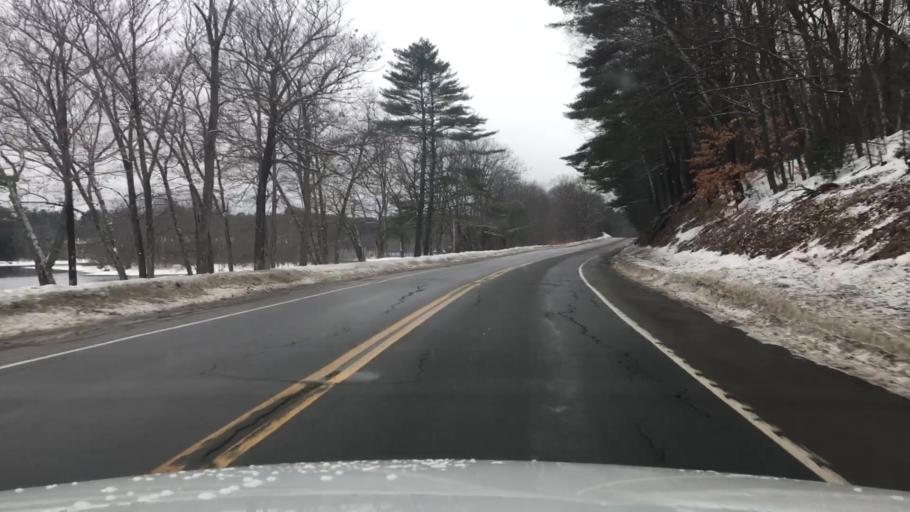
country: US
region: Maine
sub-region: Somerset County
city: Skowhegan
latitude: 44.7690
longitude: -69.6988
